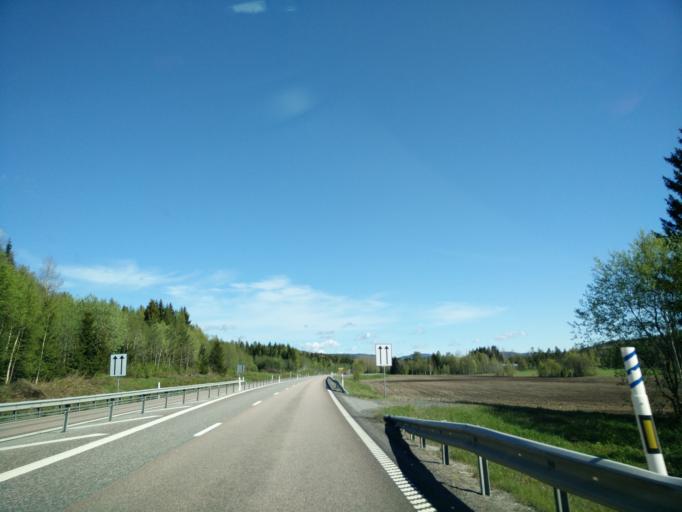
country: SE
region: Vaesternorrland
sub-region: Kramfors Kommun
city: Nordingra
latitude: 62.9750
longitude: 18.1604
